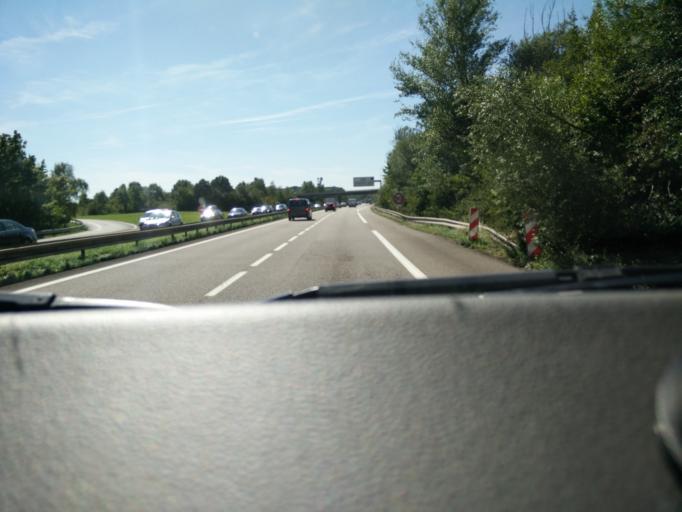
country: FR
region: Lorraine
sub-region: Departement de la Moselle
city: Entrange
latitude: 49.4348
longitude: 6.1161
